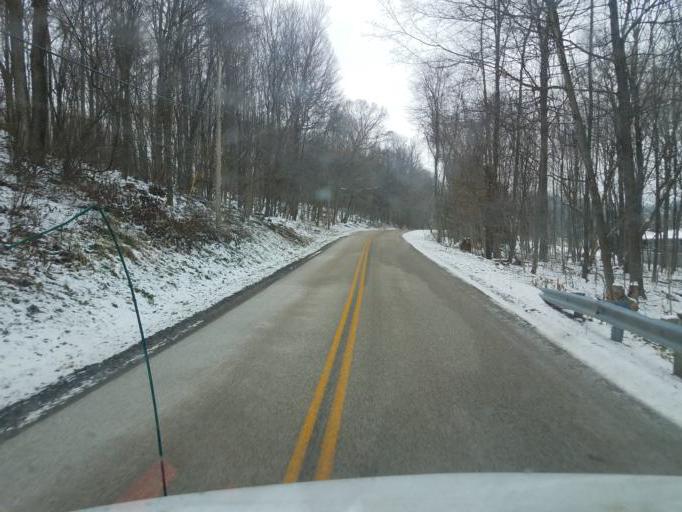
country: US
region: Ohio
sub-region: Sandusky County
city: Bellville
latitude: 40.6667
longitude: -82.4159
